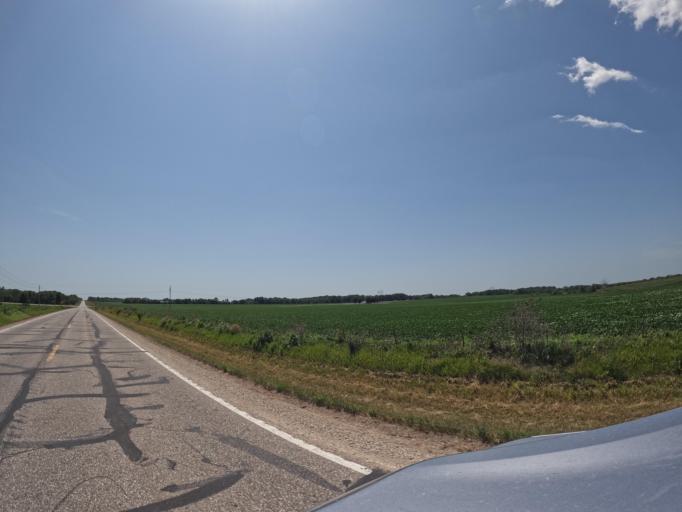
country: US
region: Iowa
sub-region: Henry County
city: Mount Pleasant
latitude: 40.9706
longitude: -91.6124
